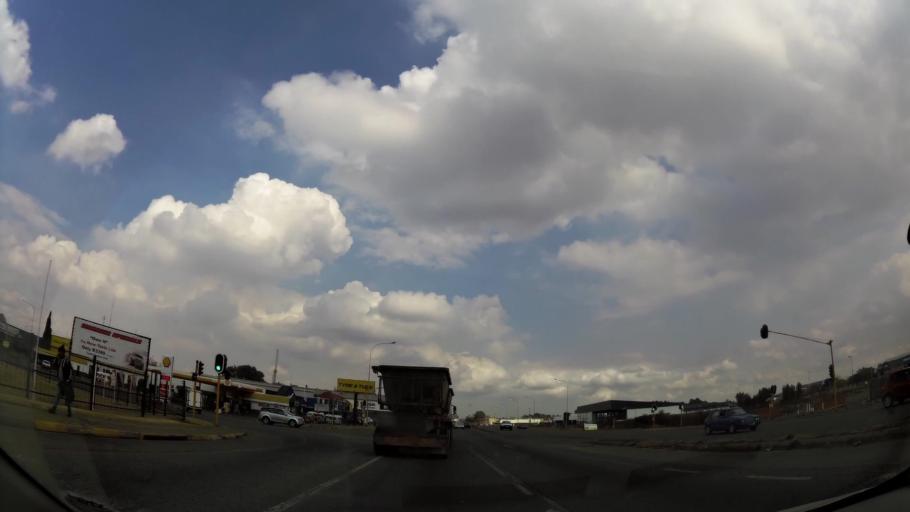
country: ZA
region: Gauteng
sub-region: Sedibeng District Municipality
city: Vereeniging
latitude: -26.6577
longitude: 27.9355
